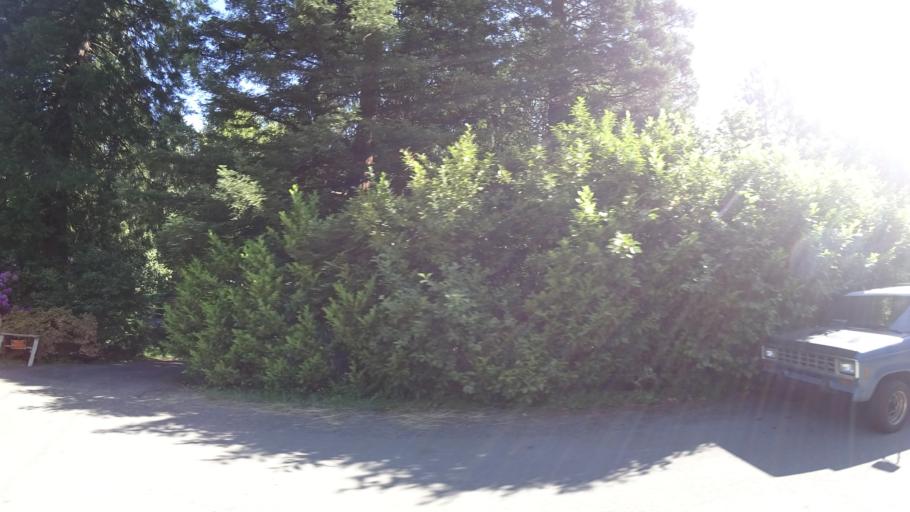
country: US
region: Oregon
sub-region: Clackamas County
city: Happy Valley
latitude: 45.4734
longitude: -122.5373
